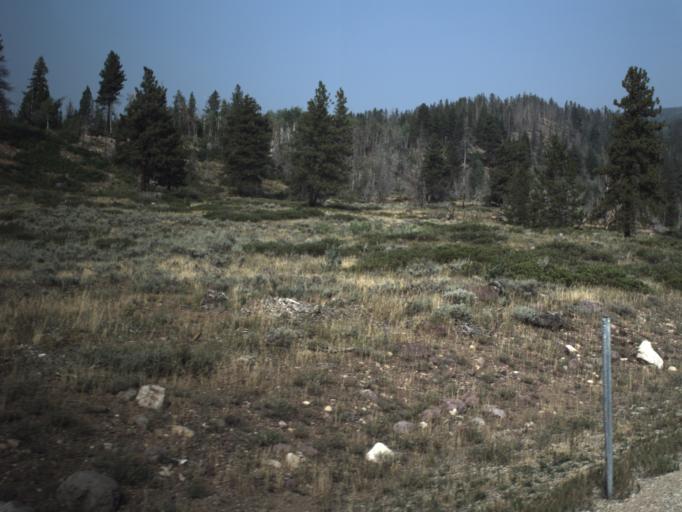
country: US
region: Utah
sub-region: Summit County
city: Francis
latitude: 40.5949
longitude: -111.0835
